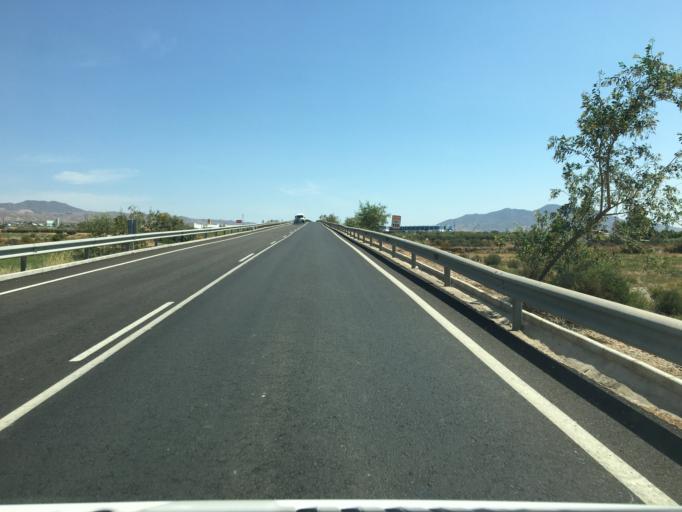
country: ES
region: Andalusia
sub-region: Provincia de Almeria
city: Huercal-Overa
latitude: 37.4257
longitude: -1.9170
